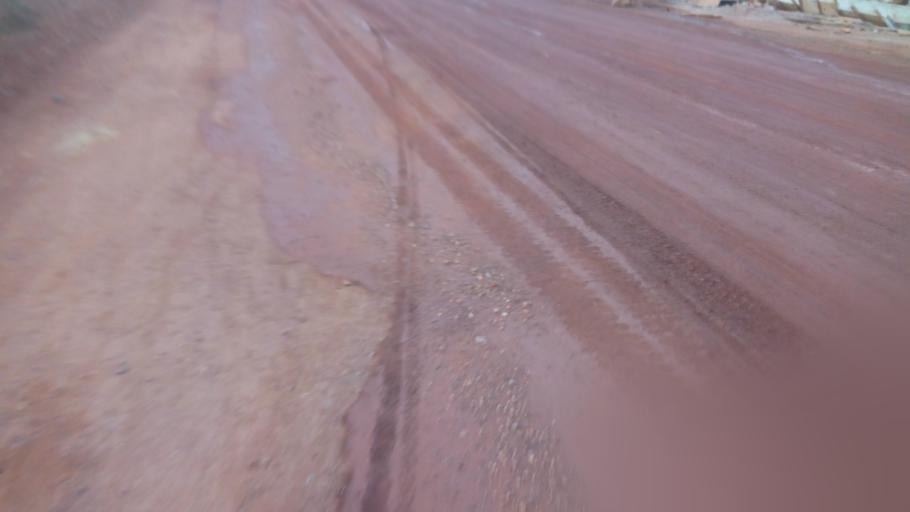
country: GH
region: Ashanti
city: Obuasi
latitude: 6.2264
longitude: -1.6823
